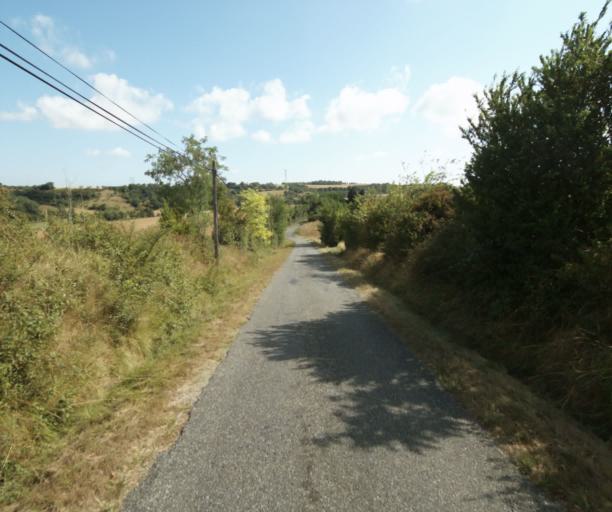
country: FR
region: Midi-Pyrenees
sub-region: Departement de la Haute-Garonne
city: Saint-Felix-Lauragais
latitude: 43.4444
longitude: 1.8242
